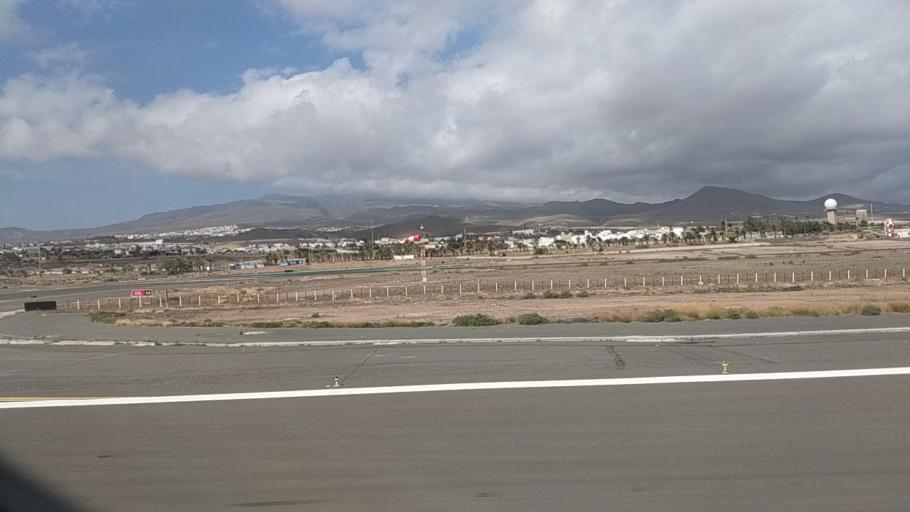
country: ES
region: Canary Islands
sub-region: Provincia de Las Palmas
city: Ingenio
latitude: 27.9189
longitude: -15.3900
